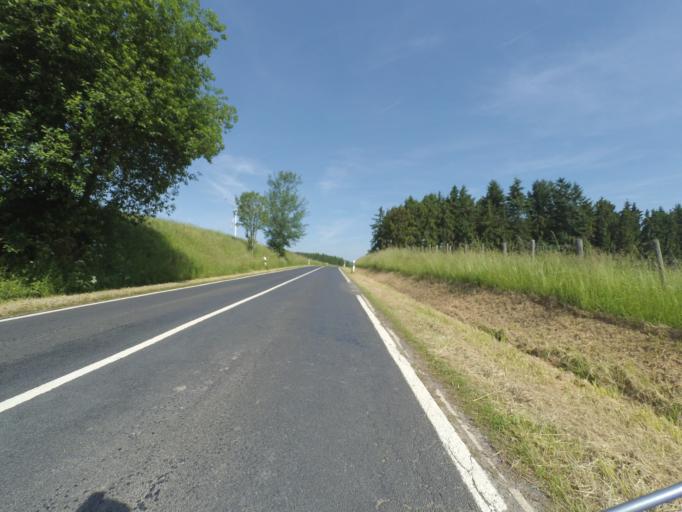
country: DE
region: Rheinland-Pfalz
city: Landkern
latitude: 50.2091
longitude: 7.1543
